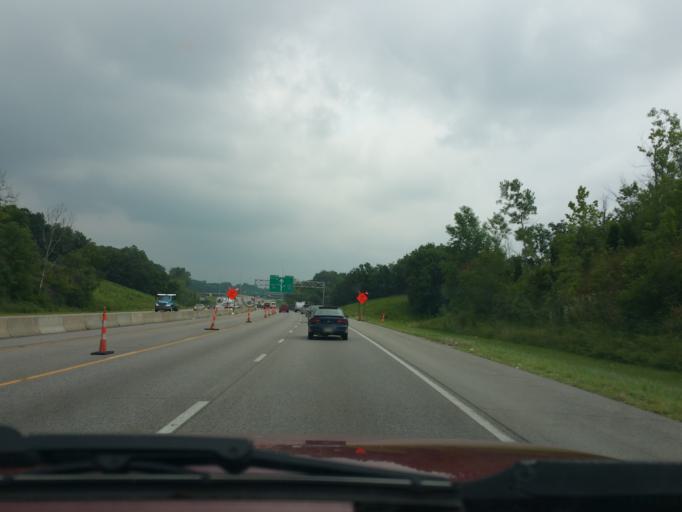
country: US
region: Kansas
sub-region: Wyandotte County
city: Kansas City
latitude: 39.1054
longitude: -94.6931
